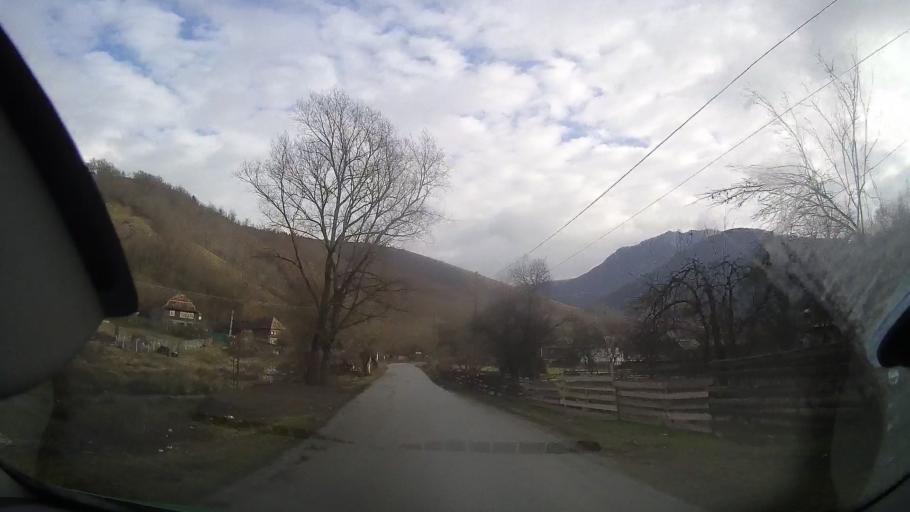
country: RO
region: Alba
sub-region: Comuna Ocolis
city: Ocolis
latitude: 46.4751
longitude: 23.4681
